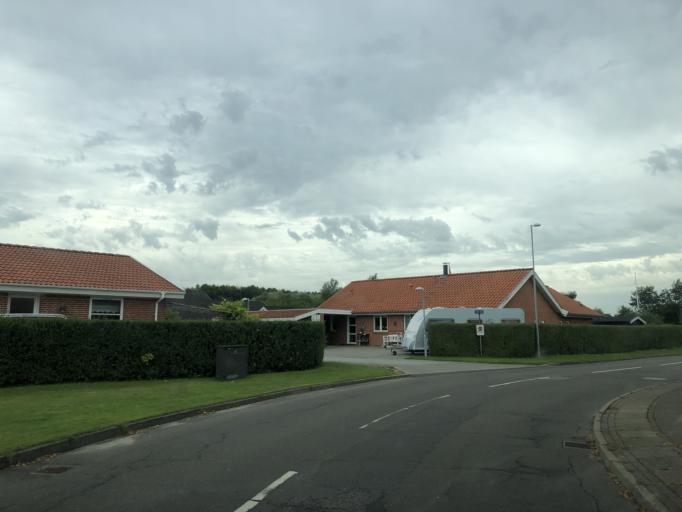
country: DK
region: Central Jutland
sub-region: Holstebro Kommune
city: Holstebro
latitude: 56.3841
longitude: 8.6003
